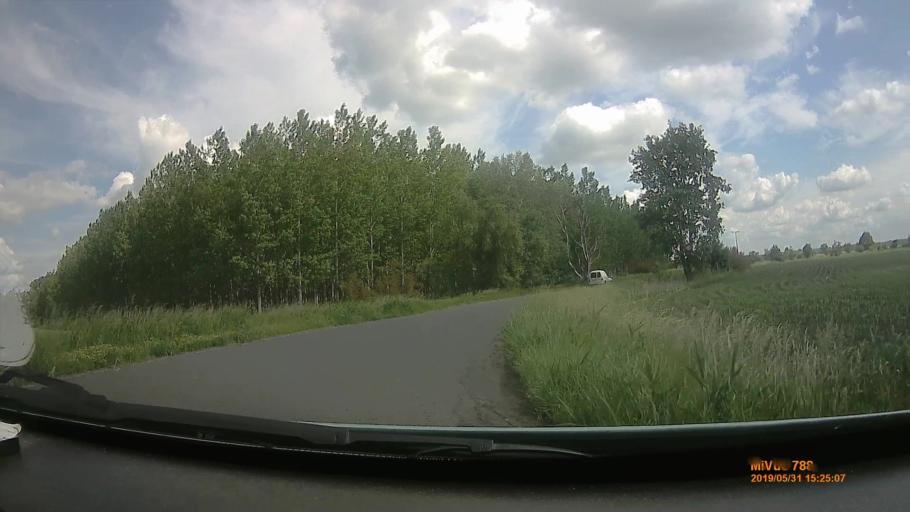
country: HU
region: Borsod-Abauj-Zemplen
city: Taktaharkany
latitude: 48.0660
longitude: 21.1636
